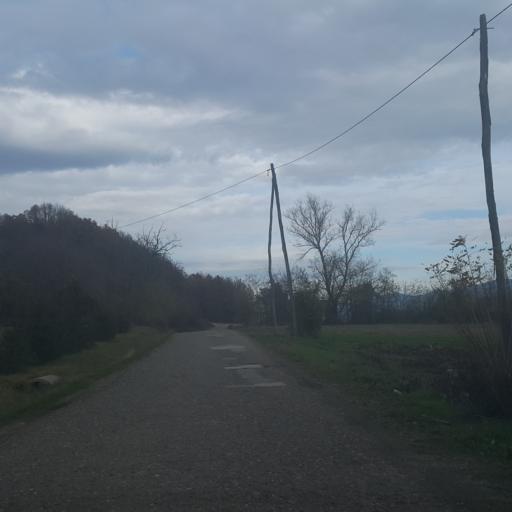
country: RS
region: Central Serbia
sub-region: Zajecarski Okrug
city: Knjazevac
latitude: 43.6074
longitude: 22.2583
